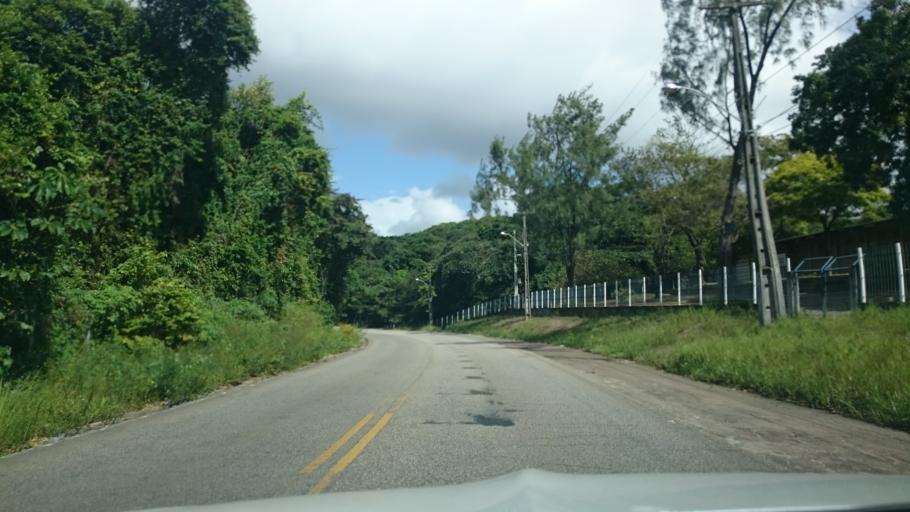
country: BR
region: Paraiba
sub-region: Joao Pessoa
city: Joao Pessoa
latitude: -7.1379
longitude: -34.8408
